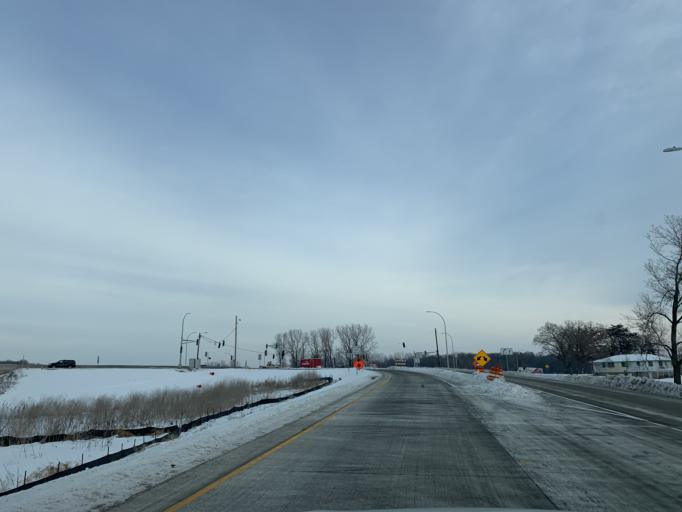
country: US
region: Minnesota
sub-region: Anoka County
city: Columbus
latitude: 45.2494
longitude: -93.0243
